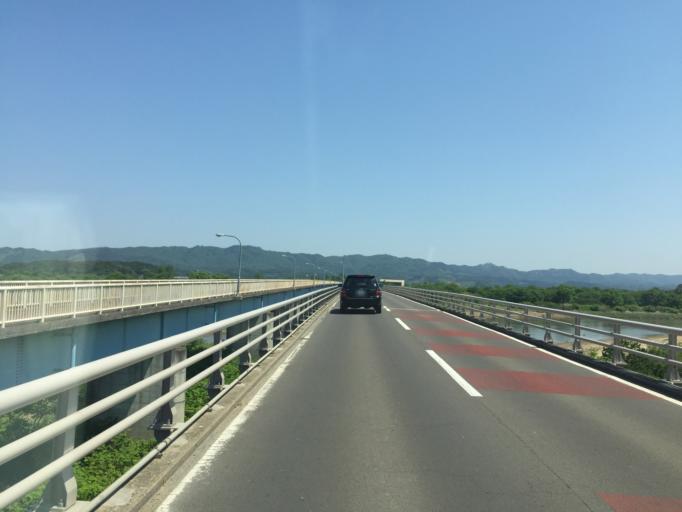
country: JP
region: Miyagi
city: Kakuda
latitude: 37.9736
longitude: 140.7973
